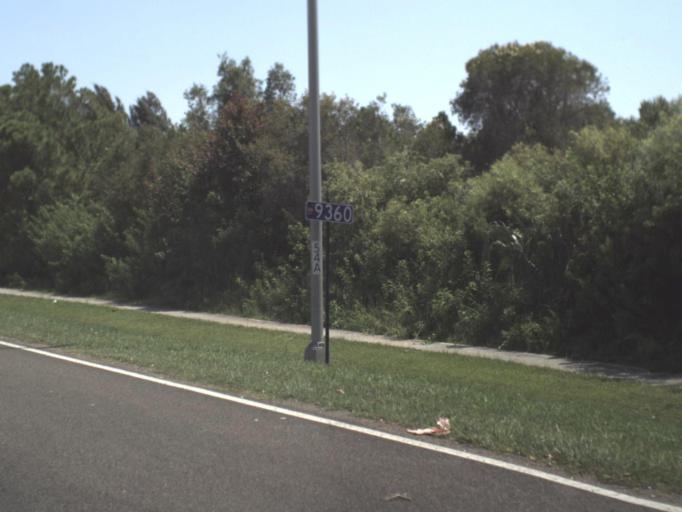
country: US
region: Florida
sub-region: Pinellas County
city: Pinellas Park
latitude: 27.8559
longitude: -82.6957
